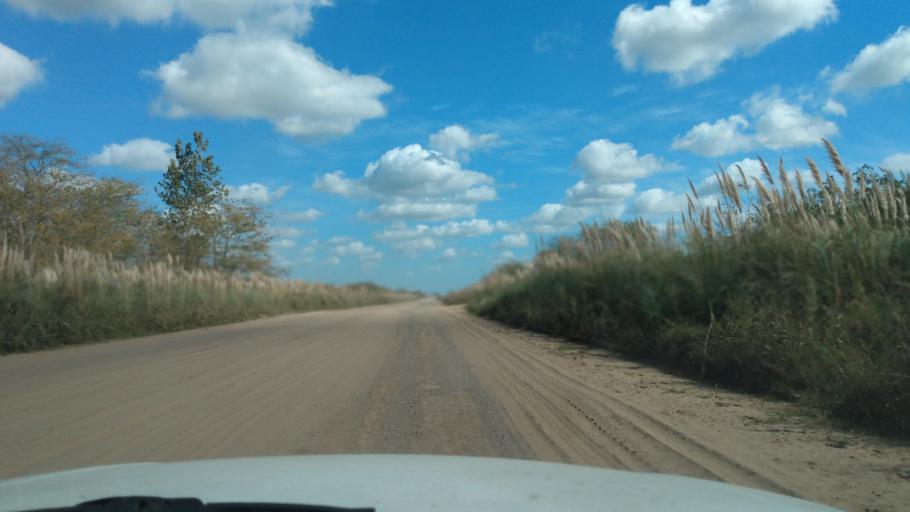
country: AR
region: Buenos Aires
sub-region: Partido de Navarro
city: Navarro
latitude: -35.0011
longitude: -59.3492
